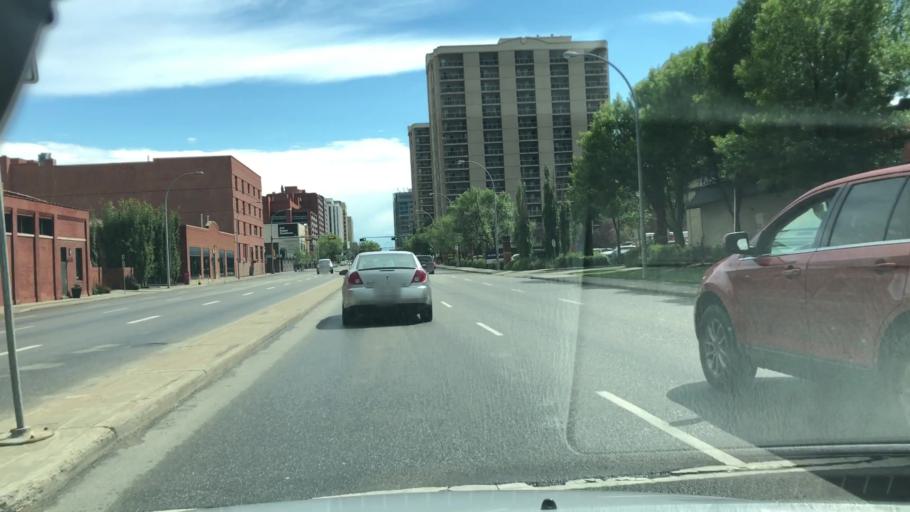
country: CA
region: Alberta
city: Edmonton
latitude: 53.5461
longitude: -113.5086
